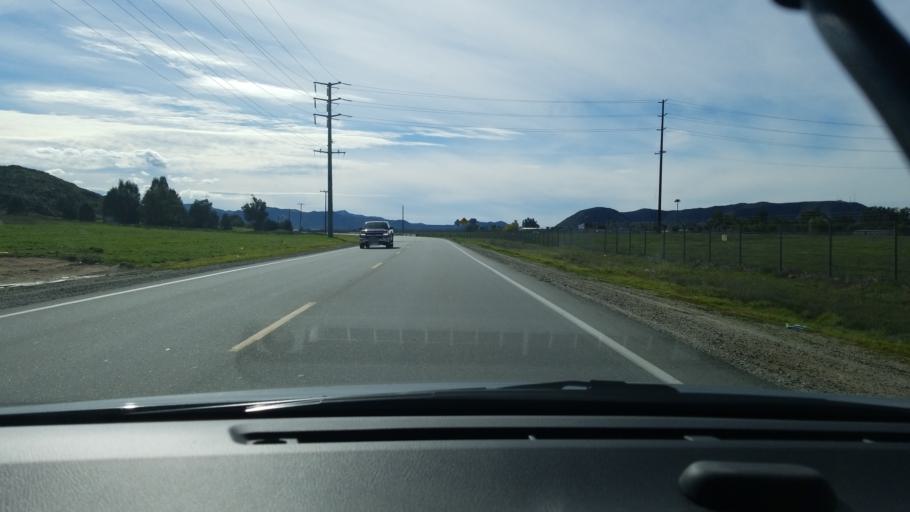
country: US
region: California
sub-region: Riverside County
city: Green Acres
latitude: 33.7595
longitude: -117.0359
